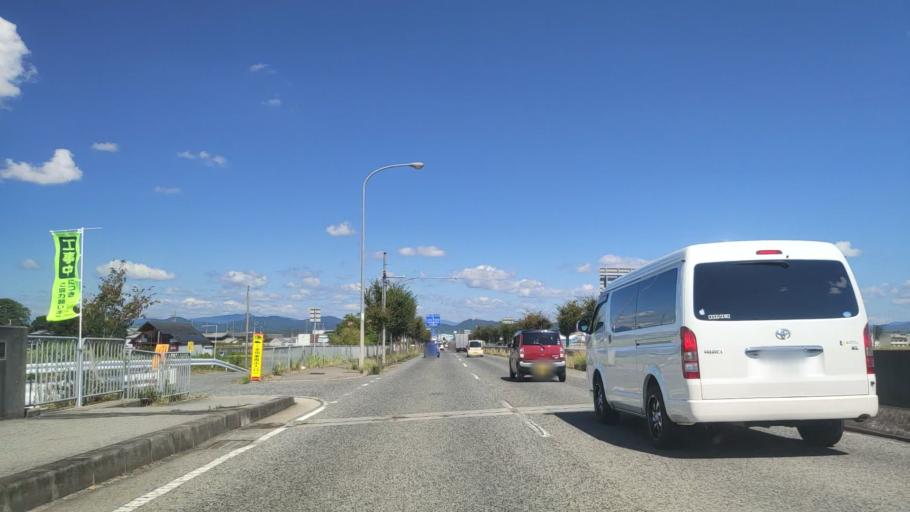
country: JP
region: Hyogo
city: Ono
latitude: 34.8795
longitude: 134.9508
